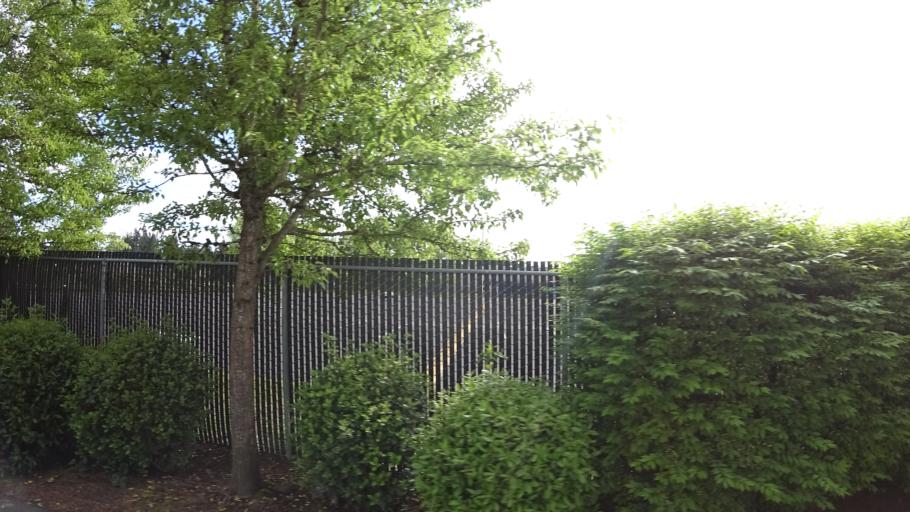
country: US
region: Oregon
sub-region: Washington County
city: Hillsboro
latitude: 45.4958
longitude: -122.9569
